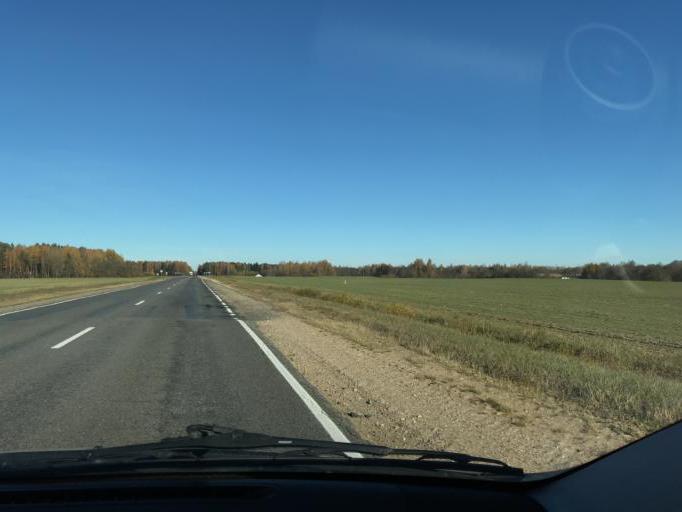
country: BY
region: Vitebsk
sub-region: Ushatski Rayon
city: Ushachy
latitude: 55.0828
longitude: 28.7555
